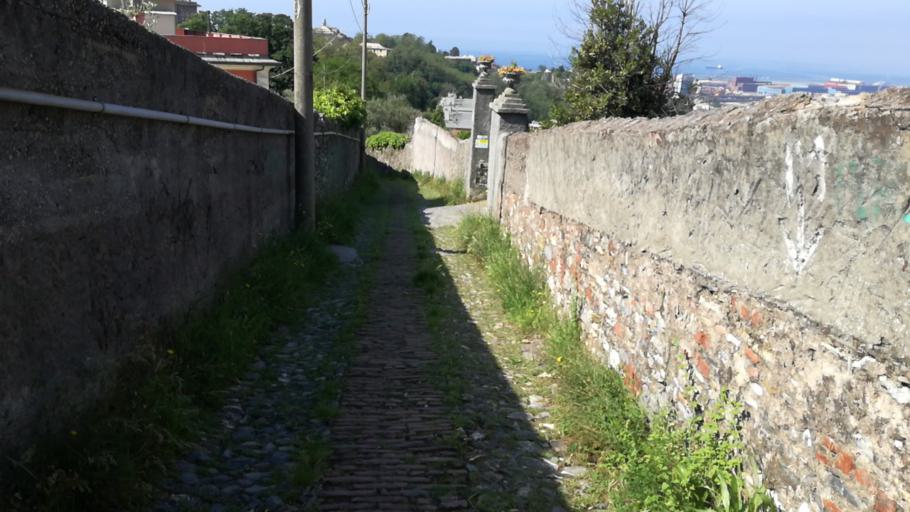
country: IT
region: Liguria
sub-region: Provincia di Genova
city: San Teodoro
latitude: 44.4230
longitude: 8.8977
